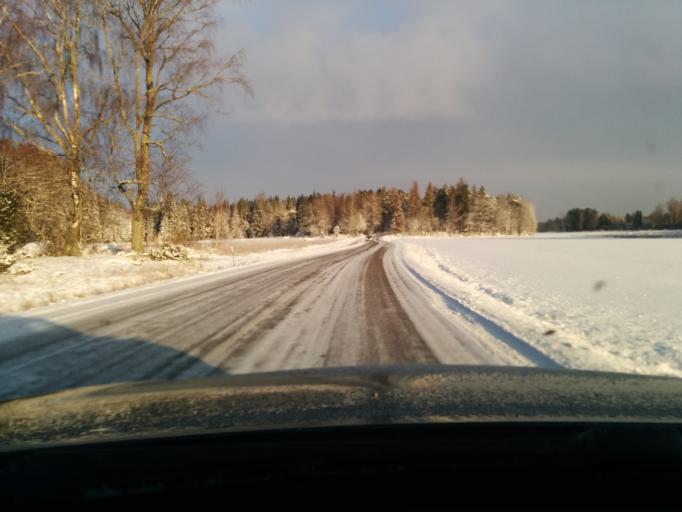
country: SE
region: Uppsala
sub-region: Tierps Kommun
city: Orbyhus
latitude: 60.1889
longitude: 17.6780
